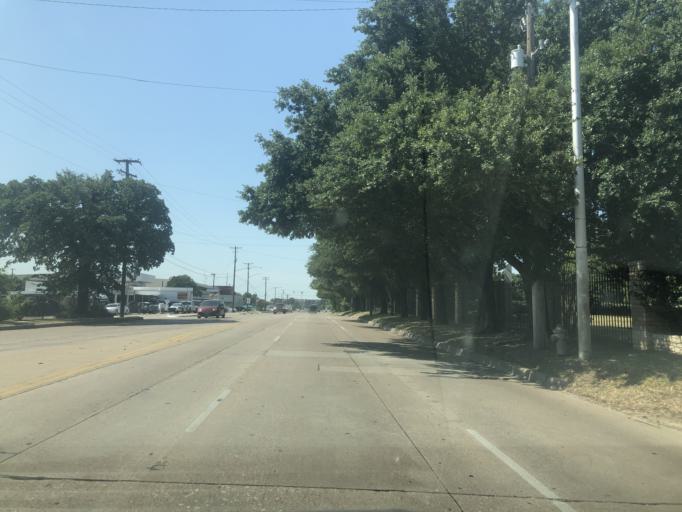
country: US
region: Texas
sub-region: Tarrant County
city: River Oaks
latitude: 32.7627
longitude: -97.3611
